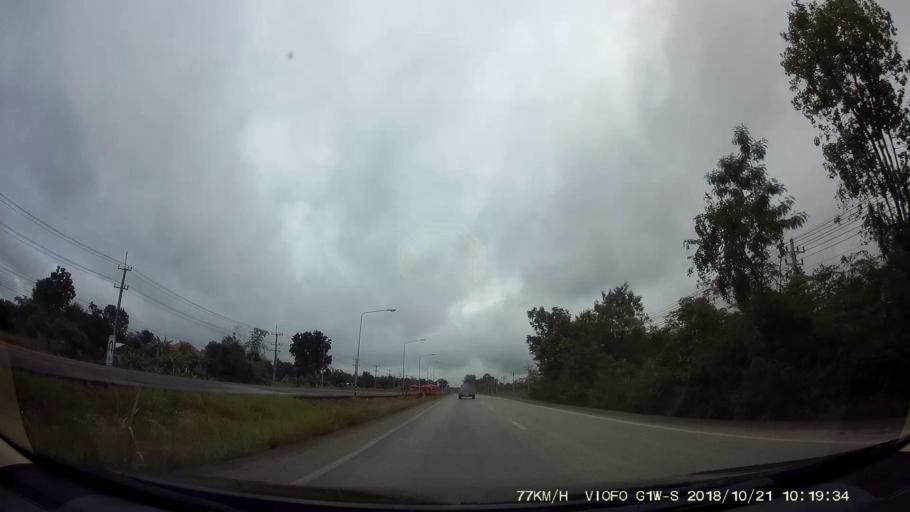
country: TH
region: Chaiyaphum
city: Phu Khiao
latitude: 16.3134
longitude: 102.1995
